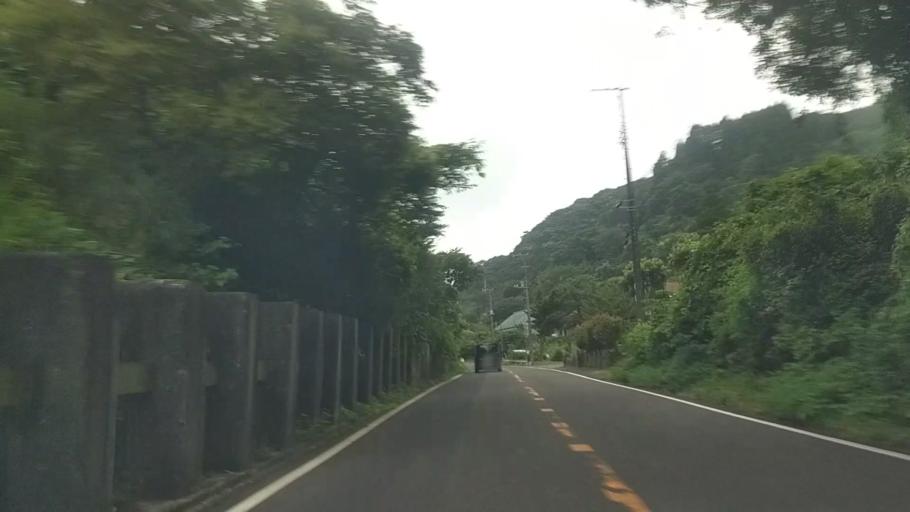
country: JP
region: Chiba
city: Kawaguchi
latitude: 35.1431
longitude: 139.9401
